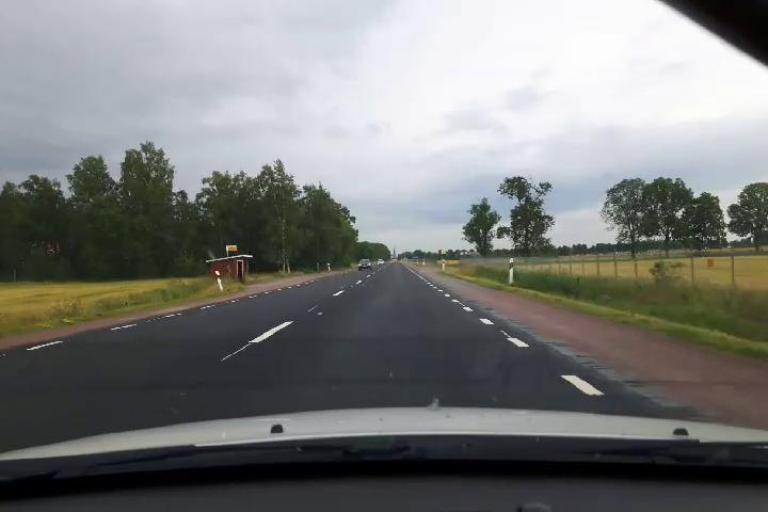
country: SE
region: Uppsala
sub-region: Uppsala Kommun
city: Gamla Uppsala
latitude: 59.8889
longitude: 17.6178
